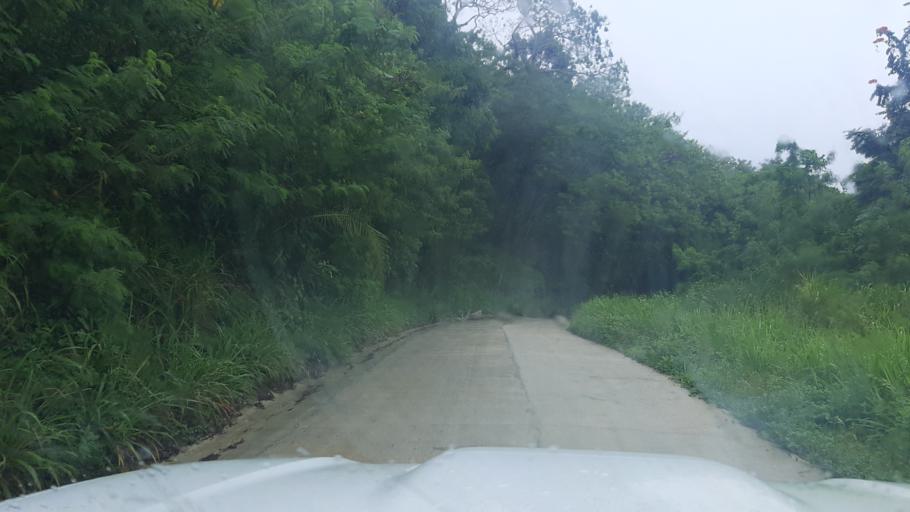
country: VU
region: Shefa
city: Port-Vila
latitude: -17.6371
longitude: 168.2110
